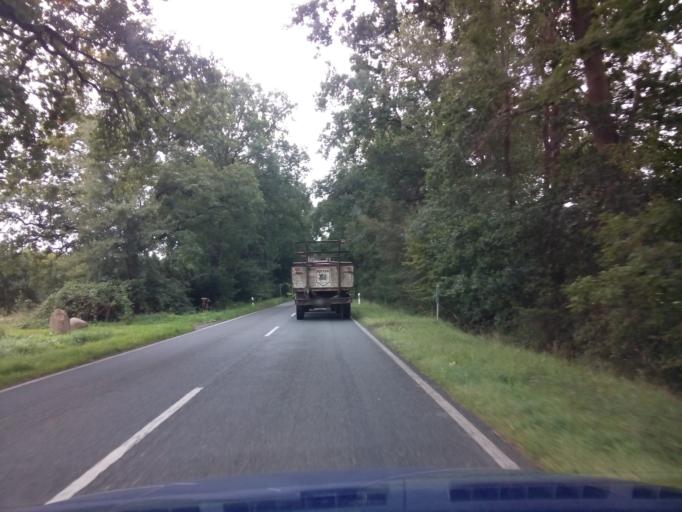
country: DE
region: Lower Saxony
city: Lubberstedt
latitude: 53.3338
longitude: 8.8182
